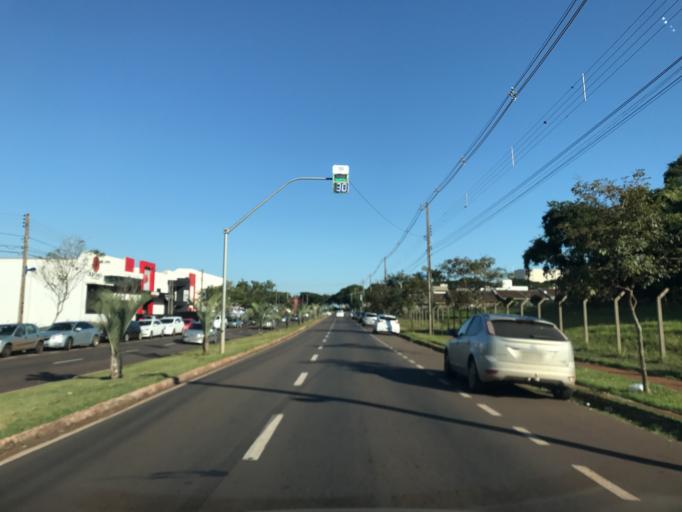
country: BR
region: Parana
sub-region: Maringa
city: Maringa
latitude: -23.4449
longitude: -51.9448
